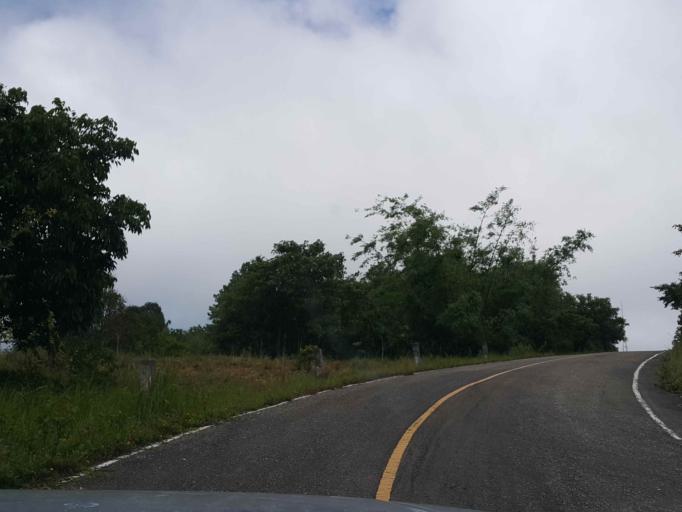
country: TH
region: Tak
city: Tak
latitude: 16.7871
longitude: 98.9245
